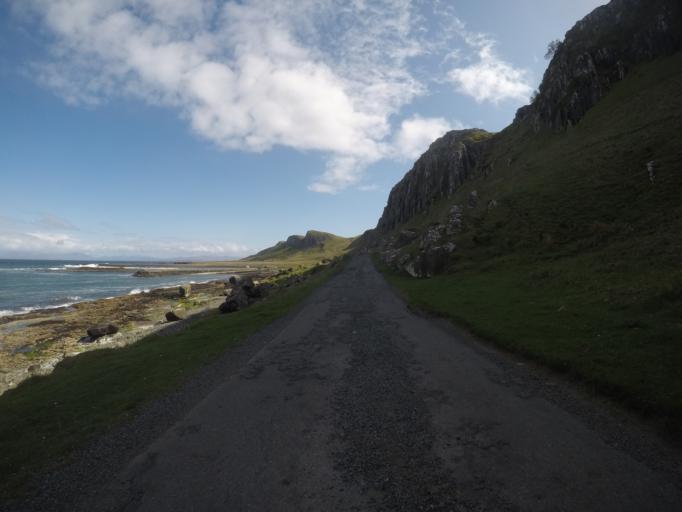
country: GB
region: Scotland
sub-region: Highland
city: Portree
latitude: 57.6353
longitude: -6.2031
